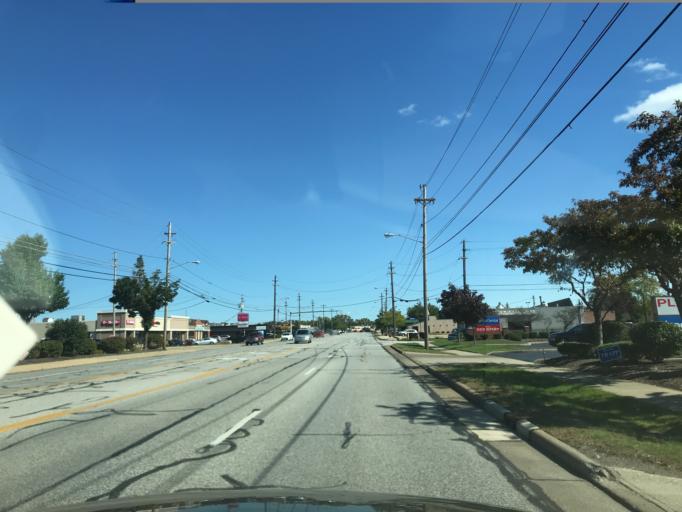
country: US
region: Ohio
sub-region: Lake County
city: Kirtland
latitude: 41.6572
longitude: -81.3699
